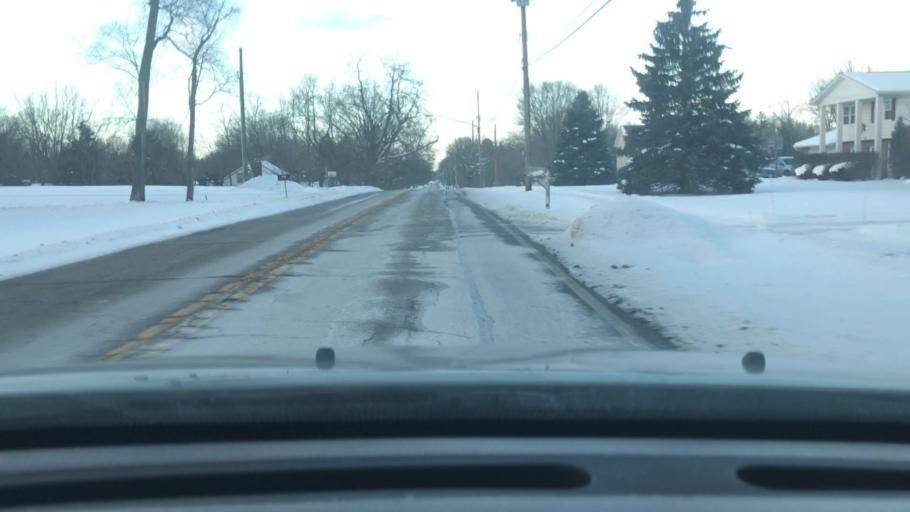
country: US
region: Ohio
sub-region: Lake County
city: Mentor
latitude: 41.6655
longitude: -81.3158
